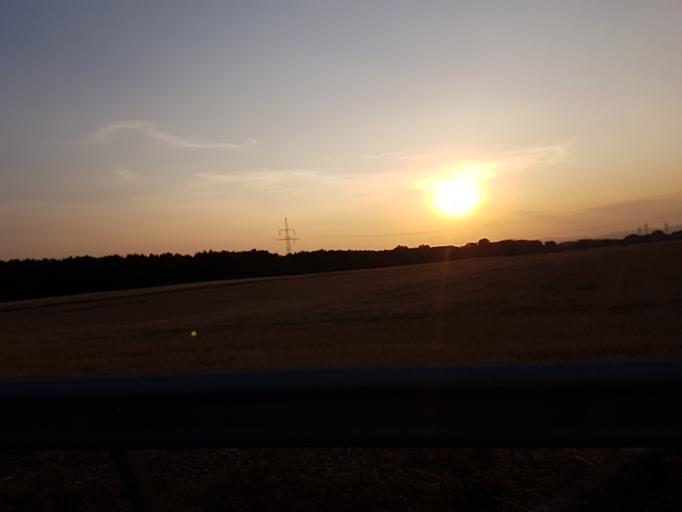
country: HU
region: Budapest
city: Budapest XVI. keruelet
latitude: 47.5416
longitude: 19.1681
